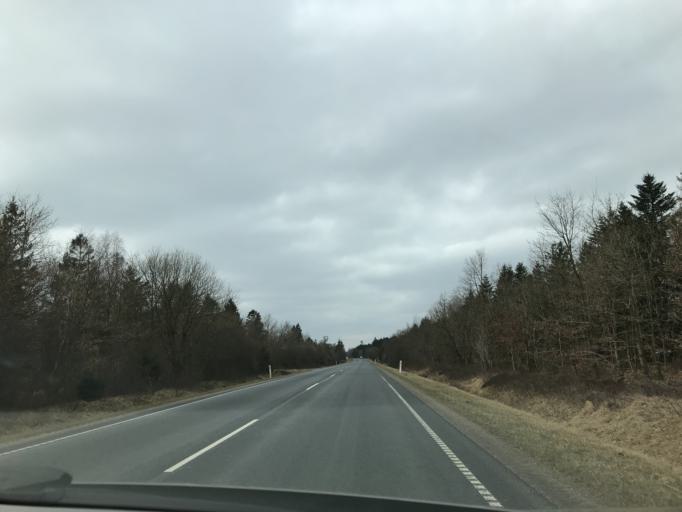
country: DK
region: South Denmark
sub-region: Billund Kommune
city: Grindsted
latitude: 55.8451
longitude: 8.8512
